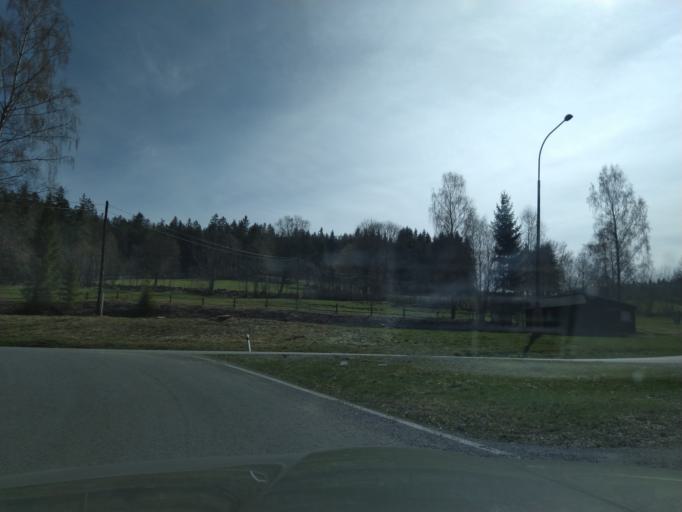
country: CZ
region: Jihocesky
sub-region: Okres Prachatice
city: Stachy
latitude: 49.0724
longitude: 13.6342
